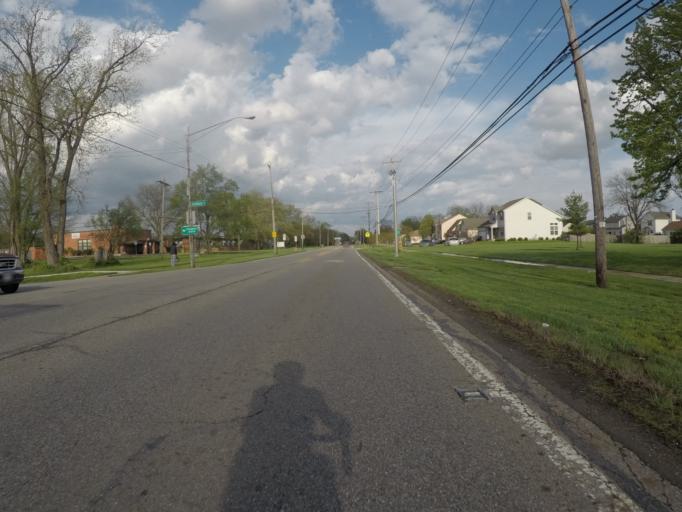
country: US
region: Ohio
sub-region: Franklin County
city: Bexley
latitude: 40.0114
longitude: -82.9461
